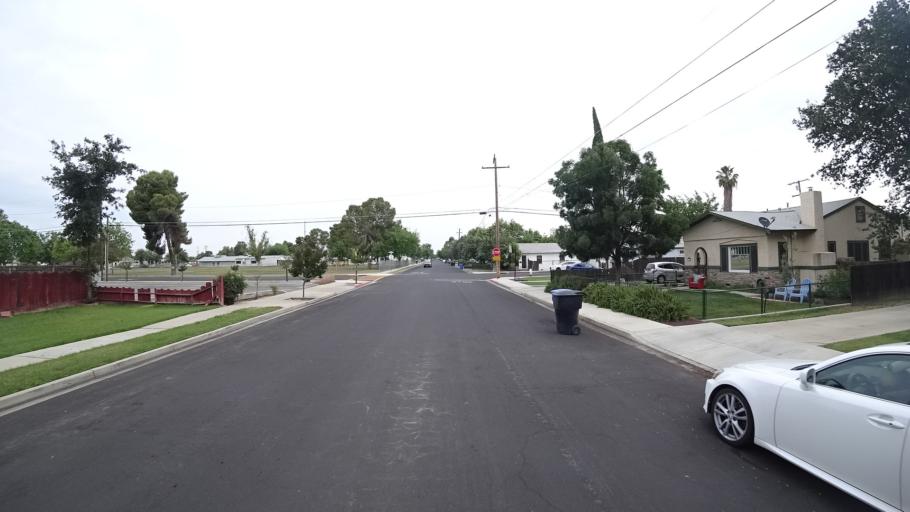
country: US
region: California
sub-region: Kings County
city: Hanford
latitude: 36.3363
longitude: -119.6522
